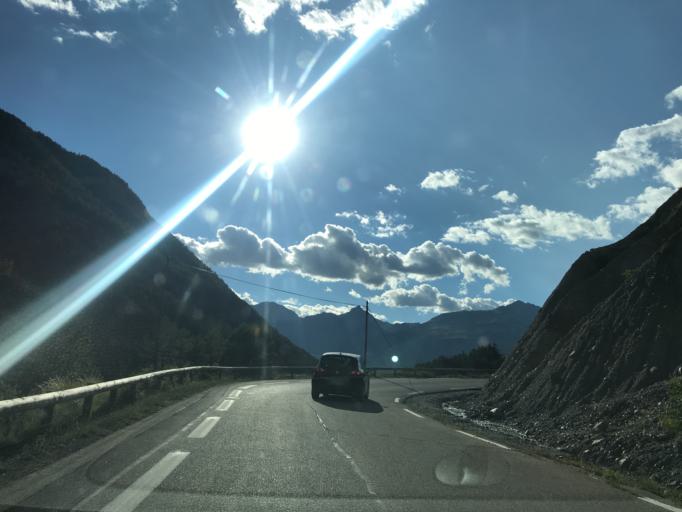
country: FR
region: Provence-Alpes-Cote d'Azur
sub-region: Departement des Hautes-Alpes
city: Briancon
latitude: 44.8803
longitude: 6.6706
